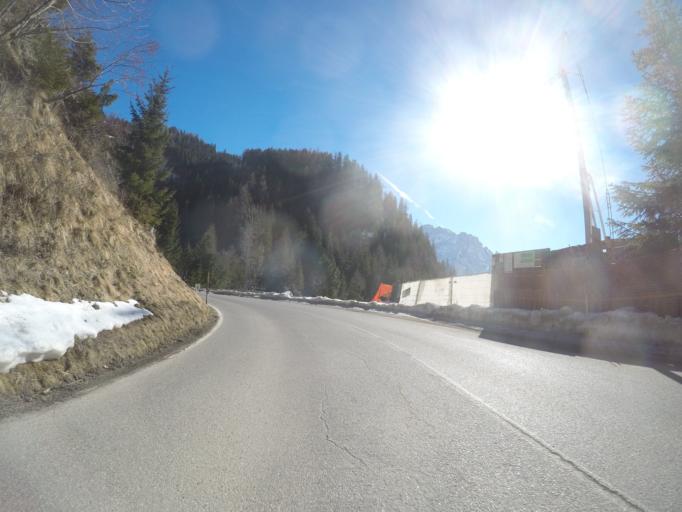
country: IT
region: Veneto
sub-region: Provincia di Belluno
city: Rocca Pietore
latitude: 46.4464
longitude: 11.9933
